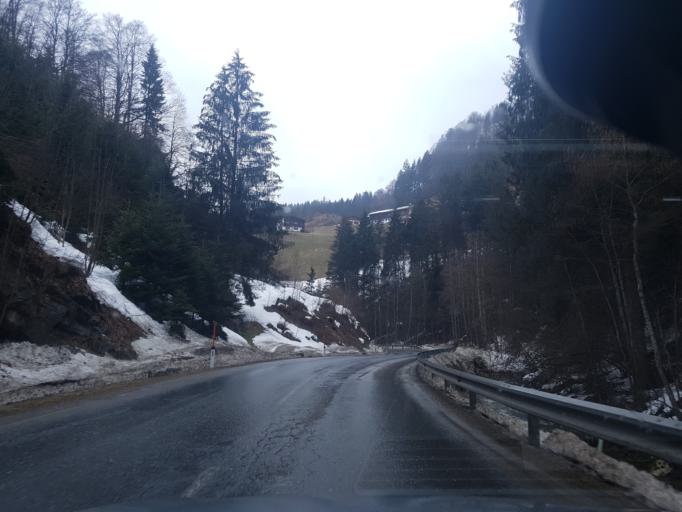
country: AT
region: Tyrol
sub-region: Politischer Bezirk Kufstein
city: Worgl
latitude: 47.4576
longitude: 12.0946
